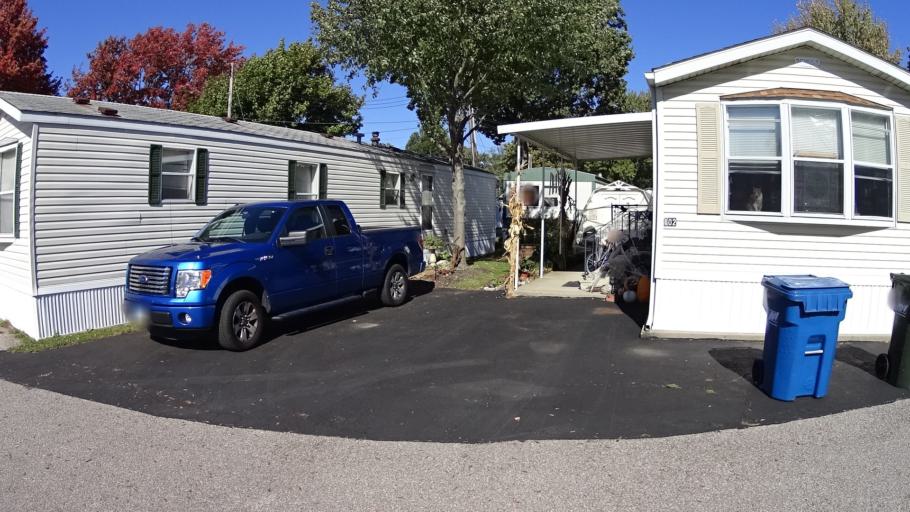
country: US
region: Ohio
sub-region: Lorain County
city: Amherst
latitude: 41.3950
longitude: -82.2491
